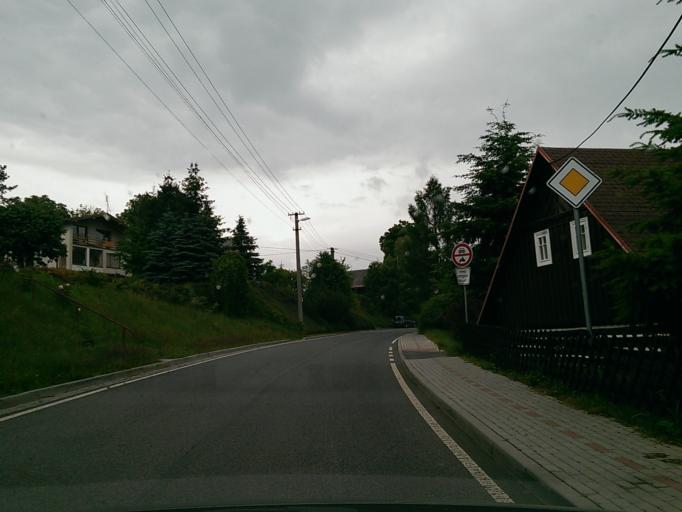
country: CZ
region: Liberecky
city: Semily
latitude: 50.6377
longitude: 15.3365
